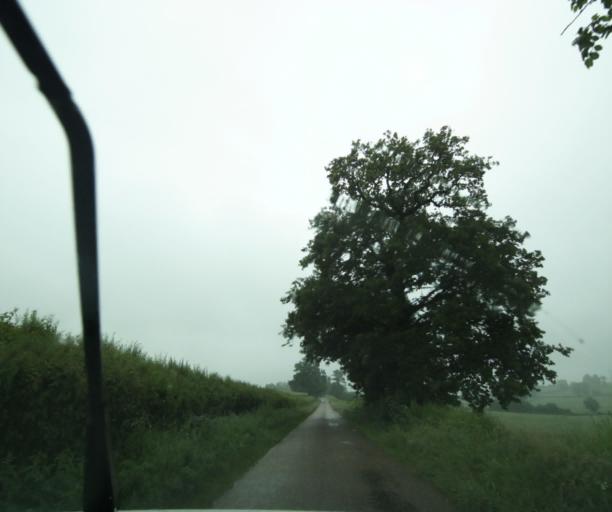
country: FR
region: Bourgogne
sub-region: Departement de Saone-et-Loire
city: Charolles
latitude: 46.3879
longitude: 4.2948
